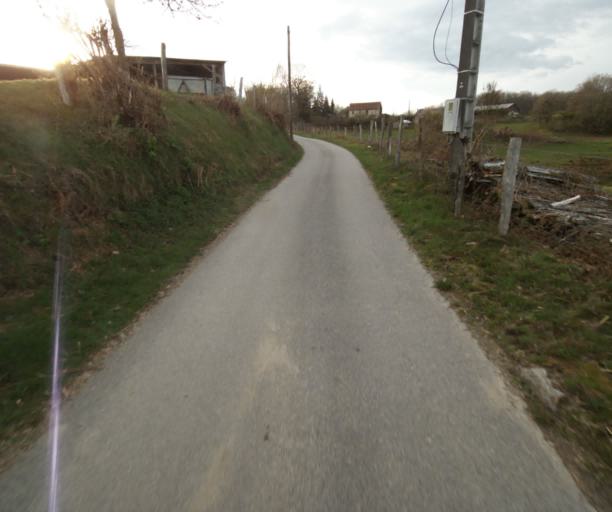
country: FR
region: Limousin
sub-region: Departement de la Correze
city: Argentat
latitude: 45.2275
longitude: 1.9526
